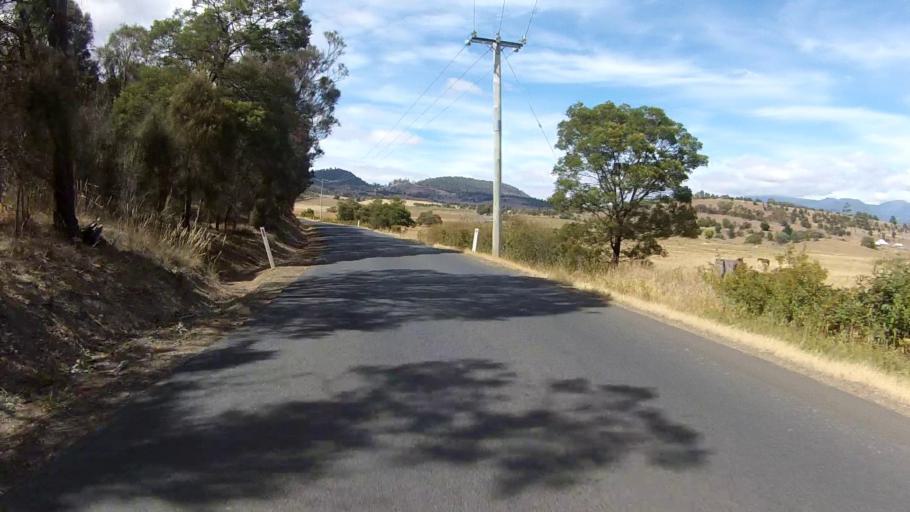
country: AU
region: Tasmania
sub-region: Brighton
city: Old Beach
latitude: -42.7488
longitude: 147.3005
